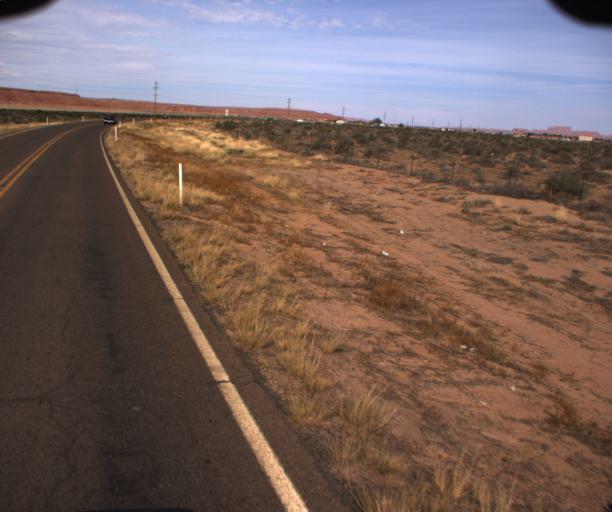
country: US
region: Arizona
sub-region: Apache County
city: Many Farms
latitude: 36.3339
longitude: -109.6238
